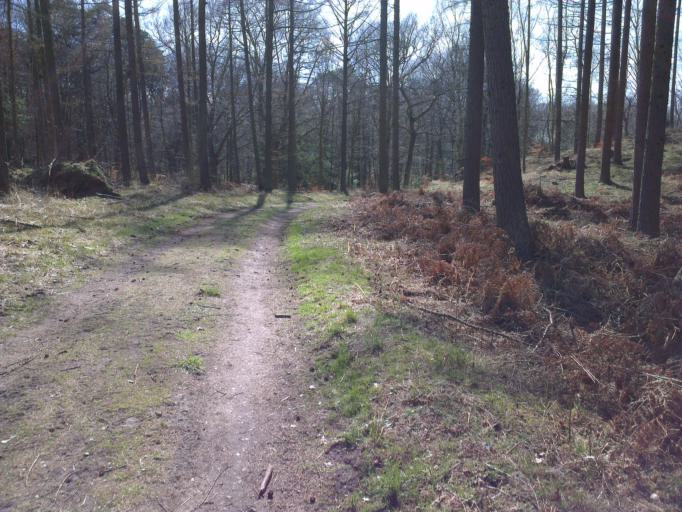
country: DK
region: Capital Region
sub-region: Frederikssund Kommune
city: Jaegerspris
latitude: 55.9225
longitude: 11.9371
